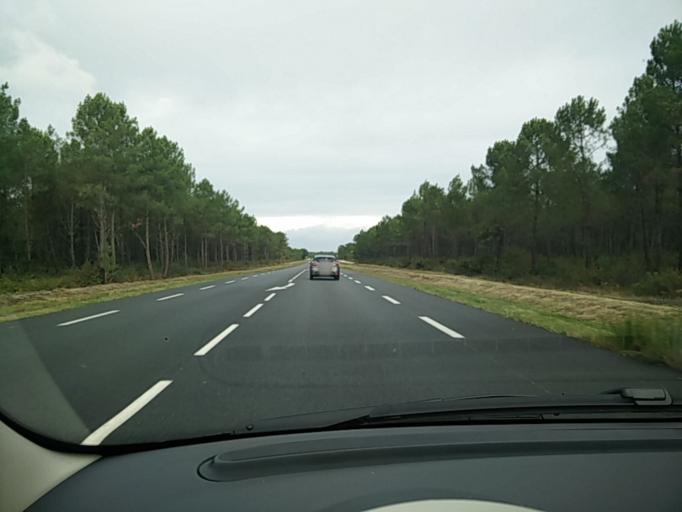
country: FR
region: Aquitaine
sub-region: Departement de la Gironde
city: Lacanau
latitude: 44.9855
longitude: -1.0689
